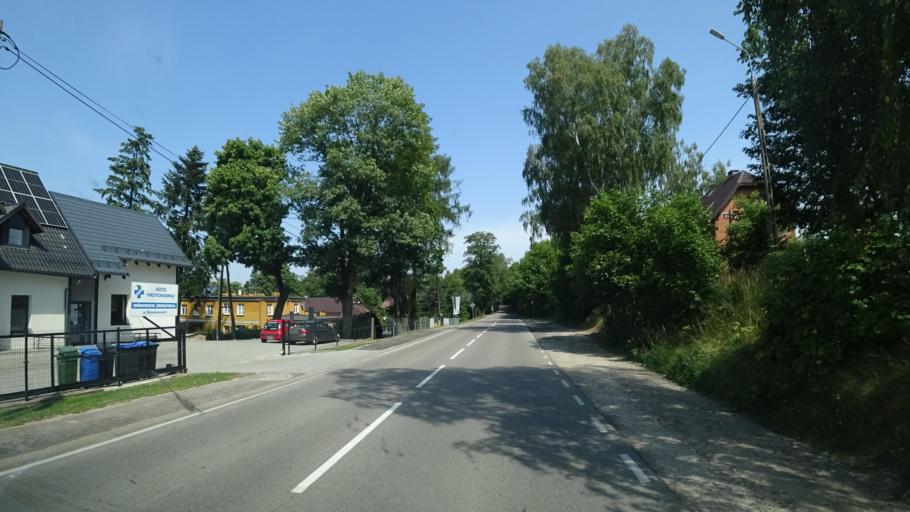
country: PL
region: Pomeranian Voivodeship
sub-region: Powiat koscierski
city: Dziemiany
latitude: 54.0108
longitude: 17.7739
